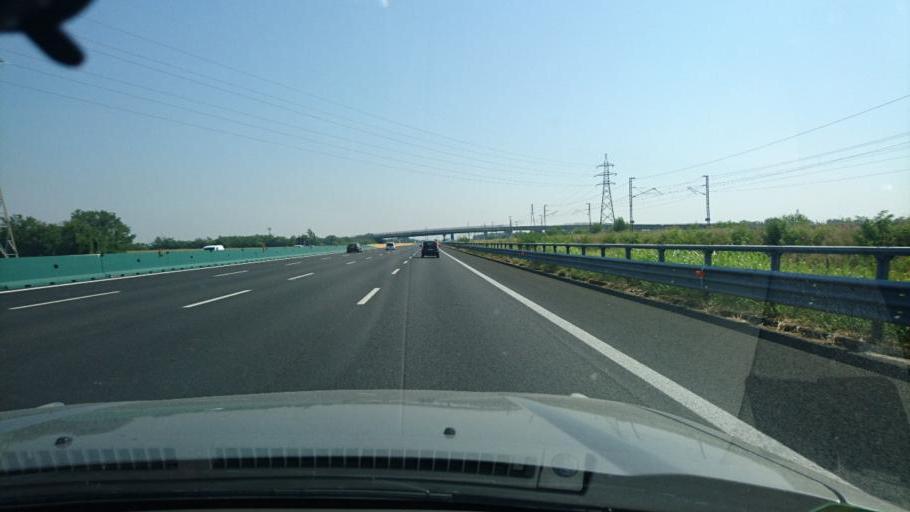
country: IT
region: Lombardy
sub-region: Citta metropolitana di Milano
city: Ossona
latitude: 45.4948
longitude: 8.8917
